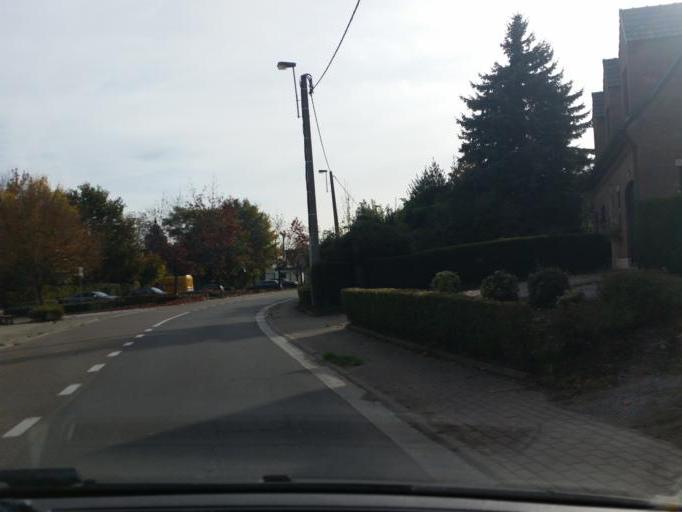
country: BE
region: Flanders
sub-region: Provincie Vlaams-Brabant
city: Grimbergen
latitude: 50.9536
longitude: 4.3622
